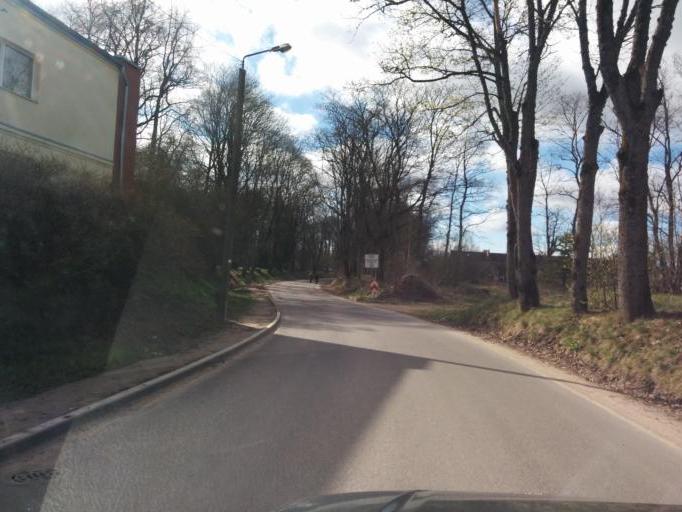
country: LV
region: Kekava
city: Balozi
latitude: 56.8910
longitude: 24.1550
